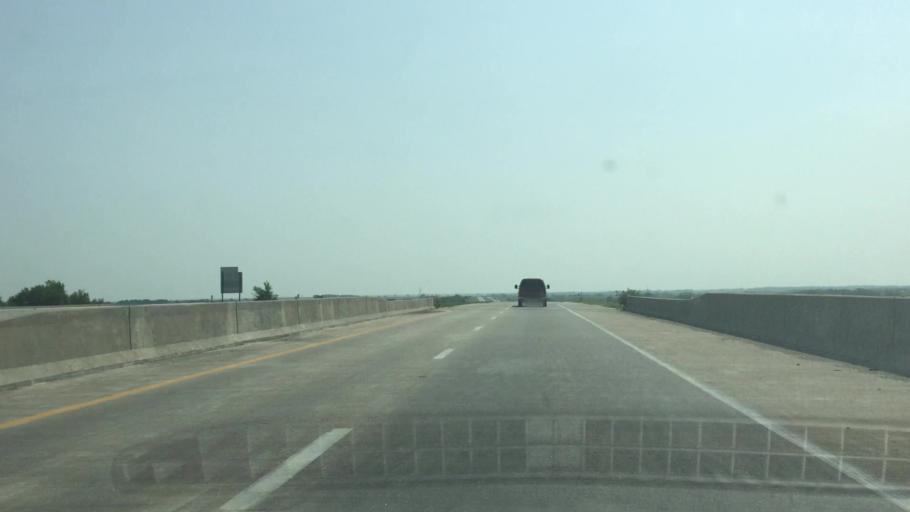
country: US
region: Kansas
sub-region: Osage County
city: Osage City
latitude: 38.4258
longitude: -95.8335
